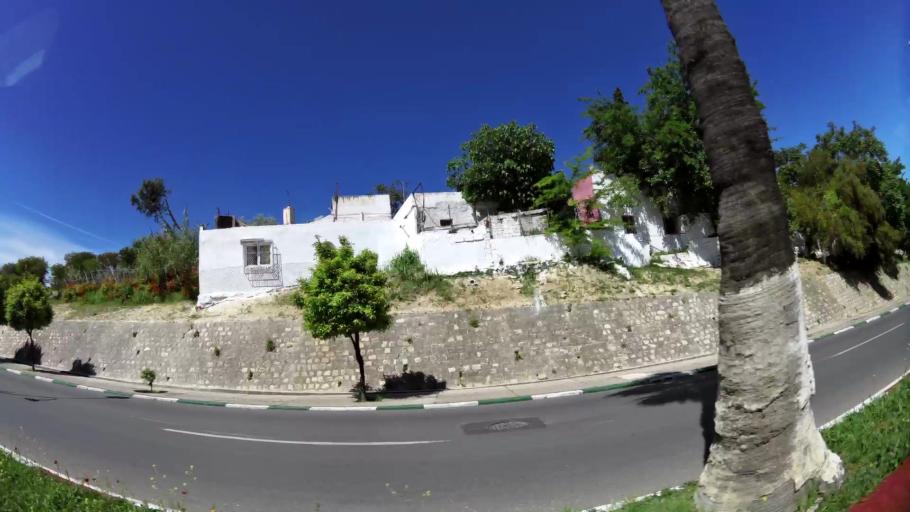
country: MA
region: Meknes-Tafilalet
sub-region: Meknes
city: Meknes
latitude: 33.8911
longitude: -5.5530
